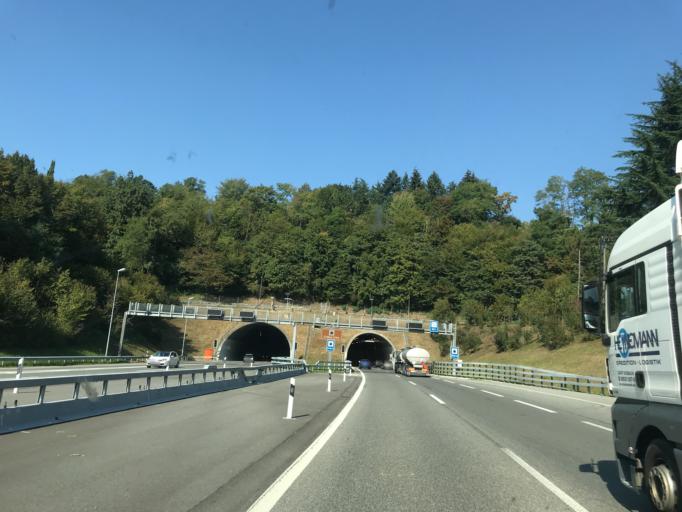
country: CH
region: Ticino
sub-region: Lugano District
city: Sorengo
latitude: 45.9875
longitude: 8.9319
